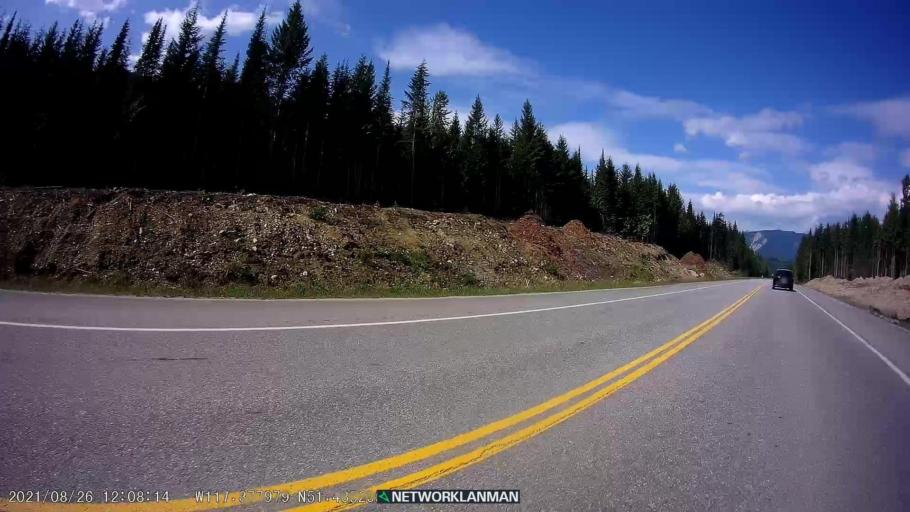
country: CA
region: British Columbia
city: Golden
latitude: 51.4854
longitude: -117.3785
